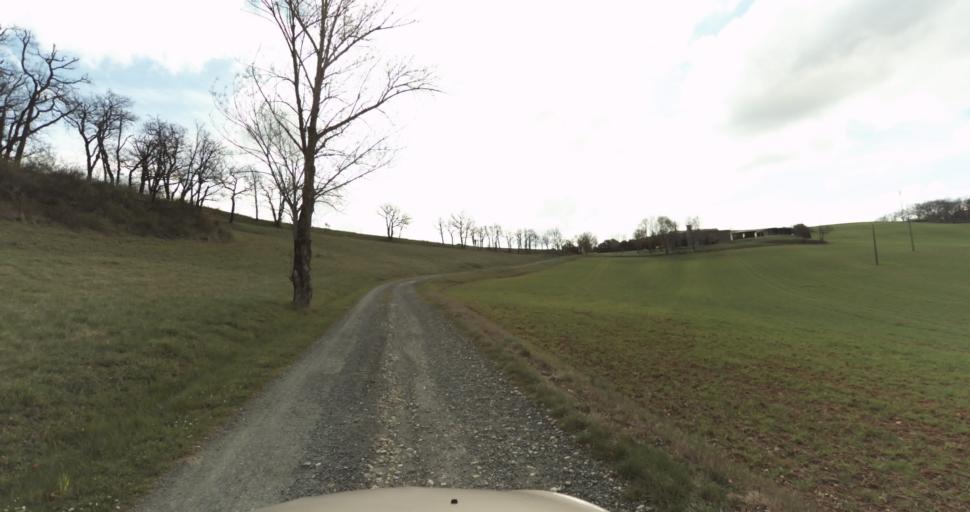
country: FR
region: Midi-Pyrenees
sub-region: Departement du Tarn
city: Puygouzon
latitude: 43.8834
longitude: 2.1592
